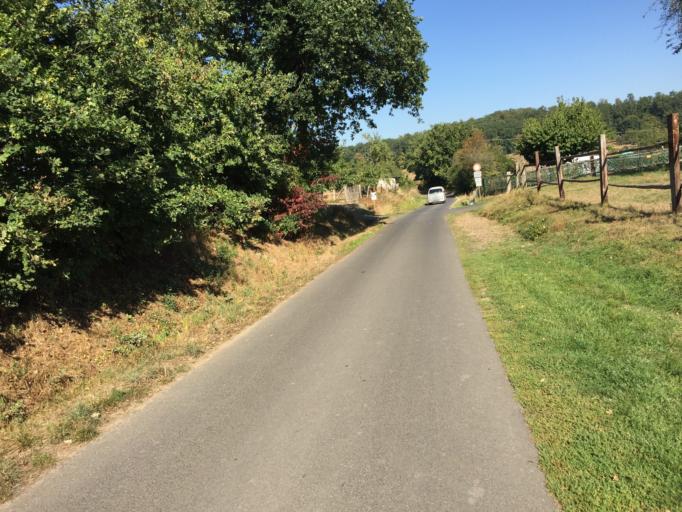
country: DE
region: Hesse
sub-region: Regierungsbezirk Darmstadt
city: Nidda
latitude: 50.4320
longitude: 8.9705
